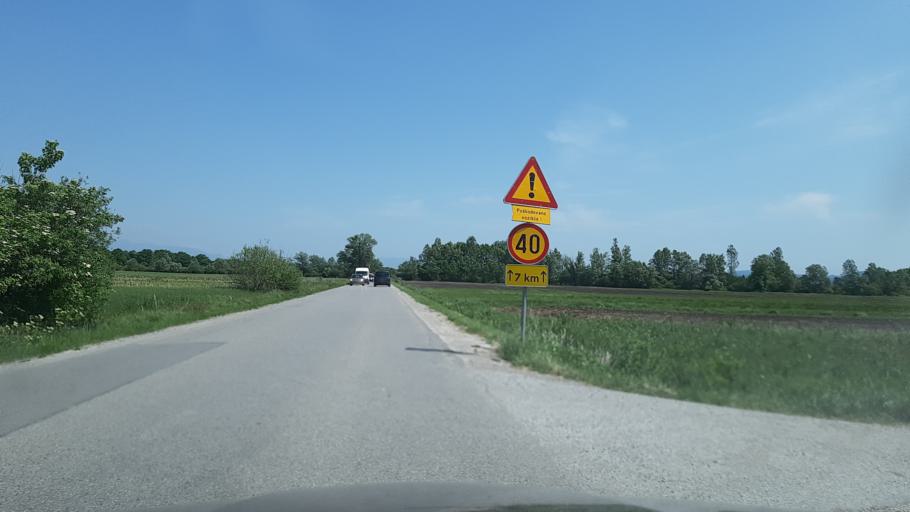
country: SI
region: Brezovica
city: Vnanje Gorice
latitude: 45.9829
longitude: 14.4346
